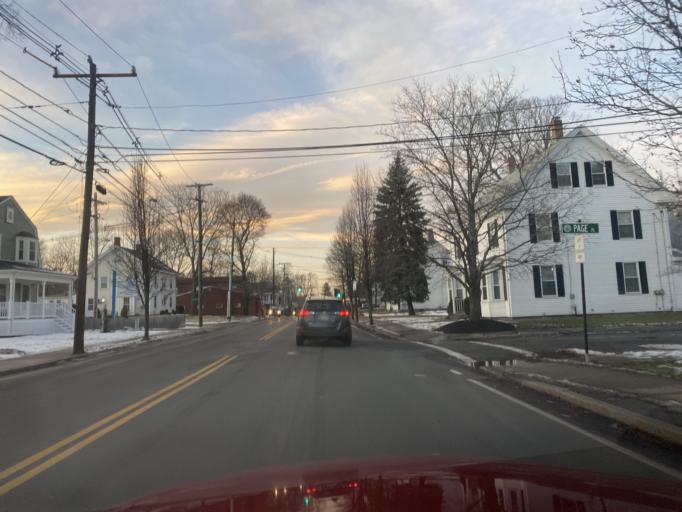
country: US
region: Massachusetts
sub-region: Middlesex County
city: Woburn
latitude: 42.4897
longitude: -71.1530
